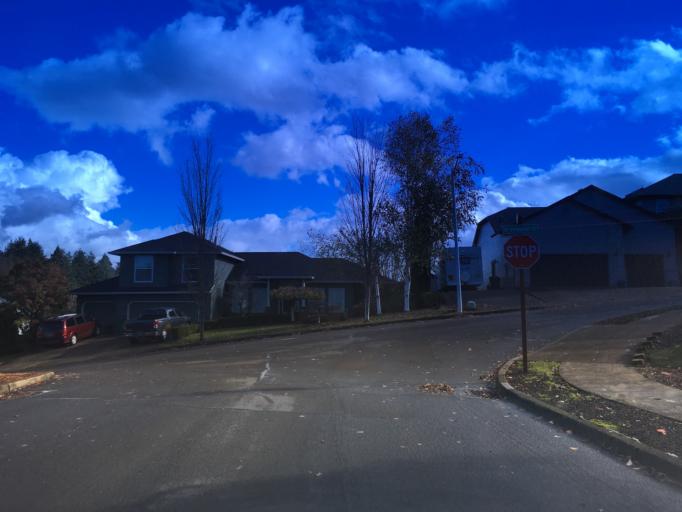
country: US
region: Oregon
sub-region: Multnomah County
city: Troutdale
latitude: 45.5085
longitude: -122.3785
